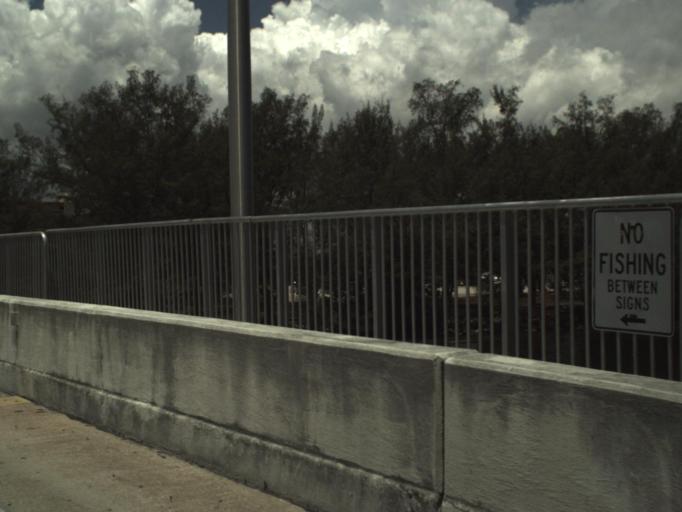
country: US
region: Florida
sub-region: Broward County
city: Lighthouse Point
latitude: 26.2503
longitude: -80.0897
